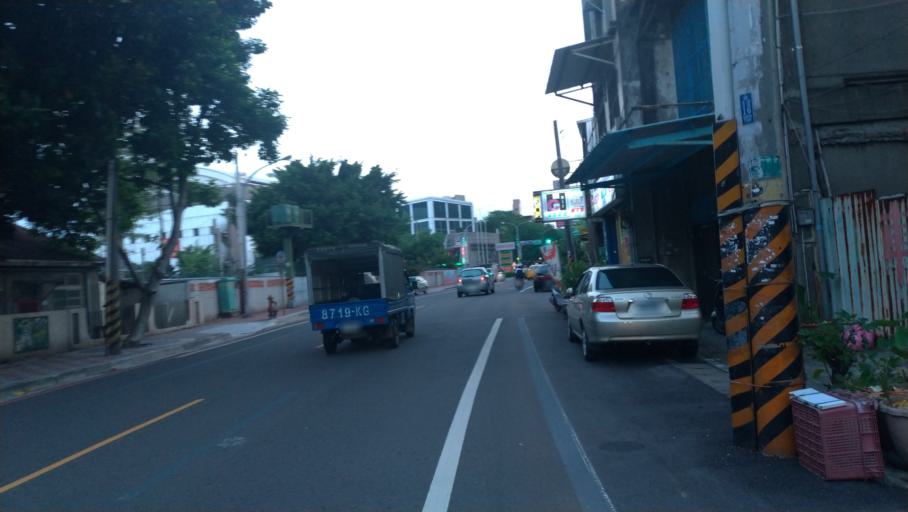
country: TW
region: Taiwan
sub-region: Taoyuan
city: Taoyuan
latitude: 24.9824
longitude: 121.3148
